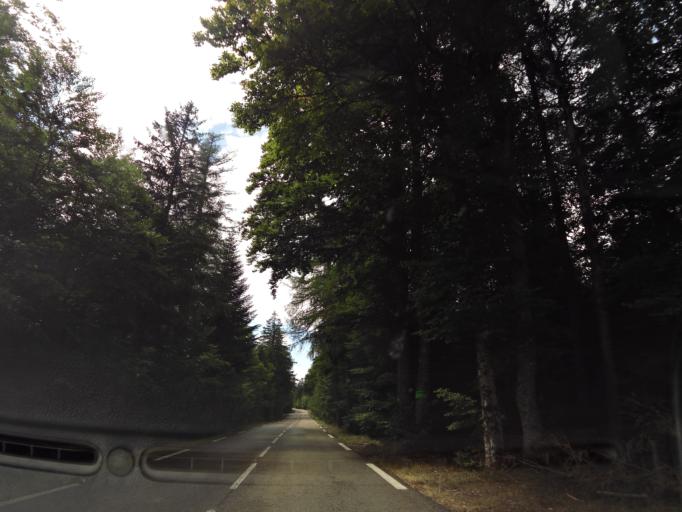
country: FR
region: Languedoc-Roussillon
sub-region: Departement de la Lozere
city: Meyrueis
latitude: 44.1042
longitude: 3.5154
